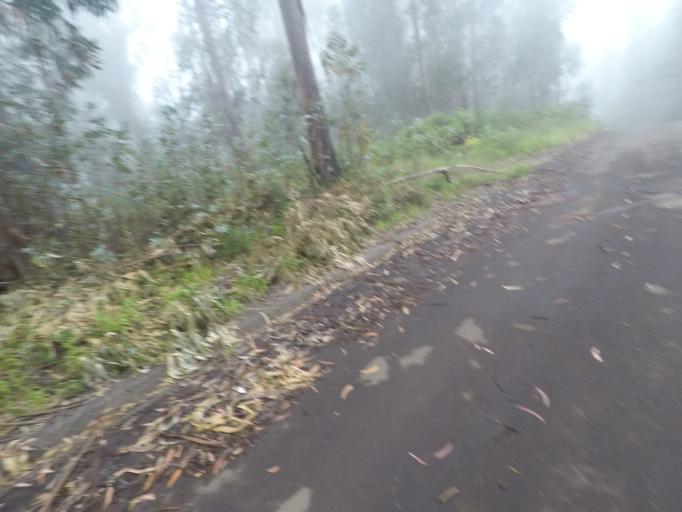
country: PT
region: Madeira
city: Ponta do Sol
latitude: 32.7125
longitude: -17.0942
